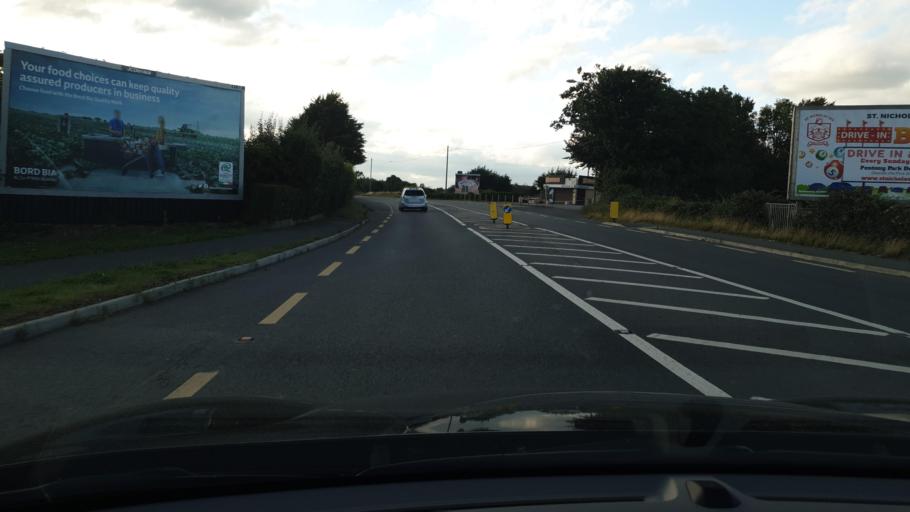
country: IE
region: Leinster
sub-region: An Mhi
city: Stamullin
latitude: 53.6578
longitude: -6.2630
